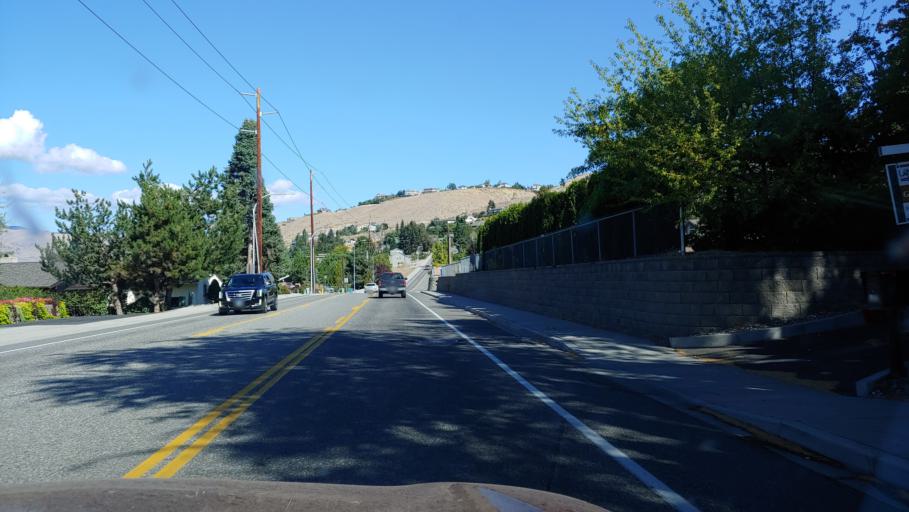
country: US
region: Washington
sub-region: Douglas County
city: East Wenatchee Bench
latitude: 47.4319
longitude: -120.2815
